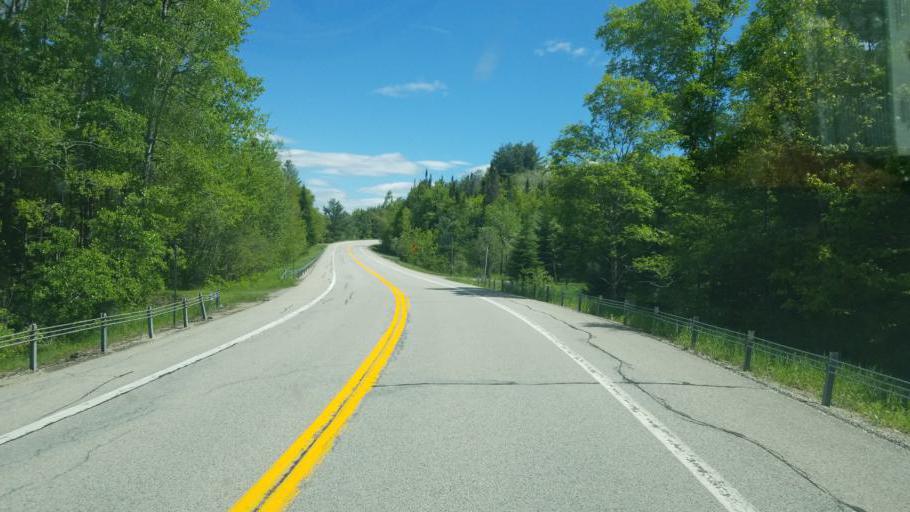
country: US
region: New York
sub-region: Hamilton County
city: Lake Pleasant
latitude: 43.2770
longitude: -74.5538
